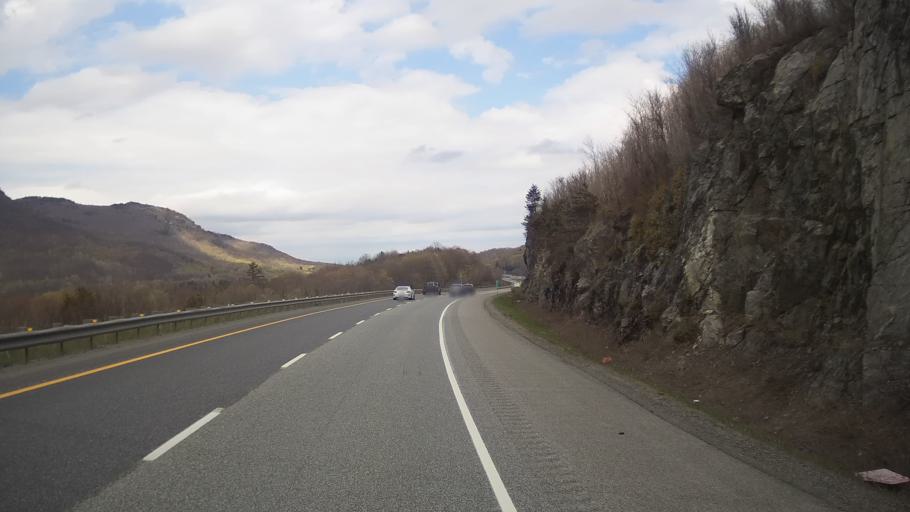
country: CA
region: Quebec
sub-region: Estrie
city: Magog
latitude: 45.2896
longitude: -72.2652
